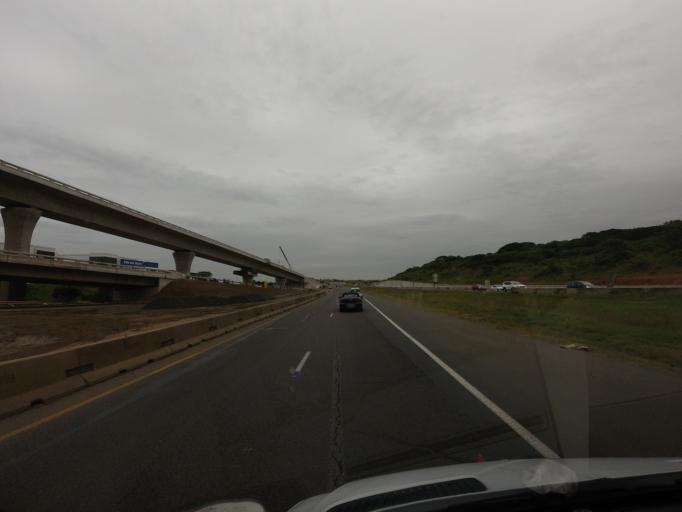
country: ZA
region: KwaZulu-Natal
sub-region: eThekwini Metropolitan Municipality
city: Durban
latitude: -29.7254
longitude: 31.0580
